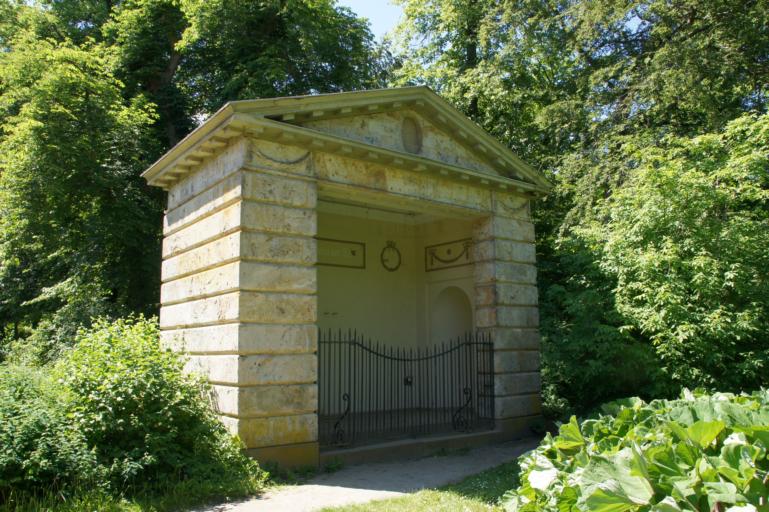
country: DE
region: Schleswig-Holstein
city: Eutin
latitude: 54.1355
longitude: 10.6225
